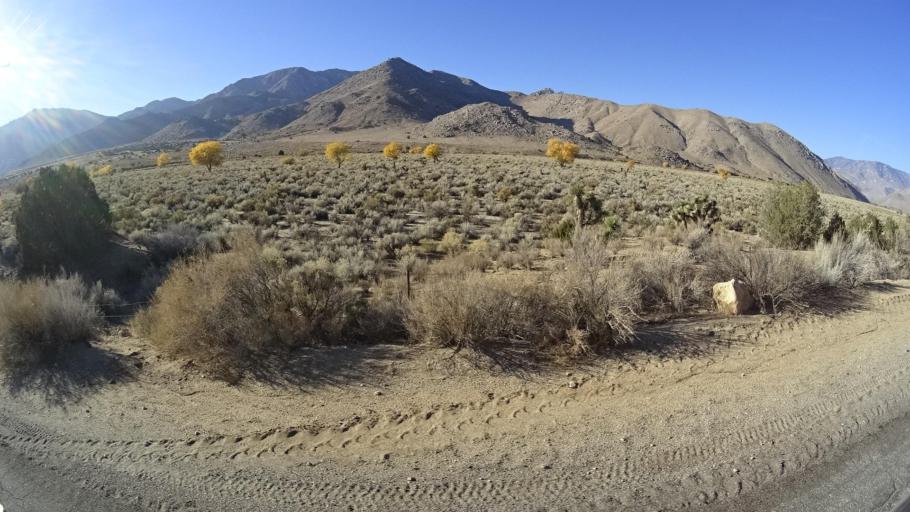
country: US
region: California
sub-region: Kern County
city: Weldon
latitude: 35.5836
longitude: -118.2441
